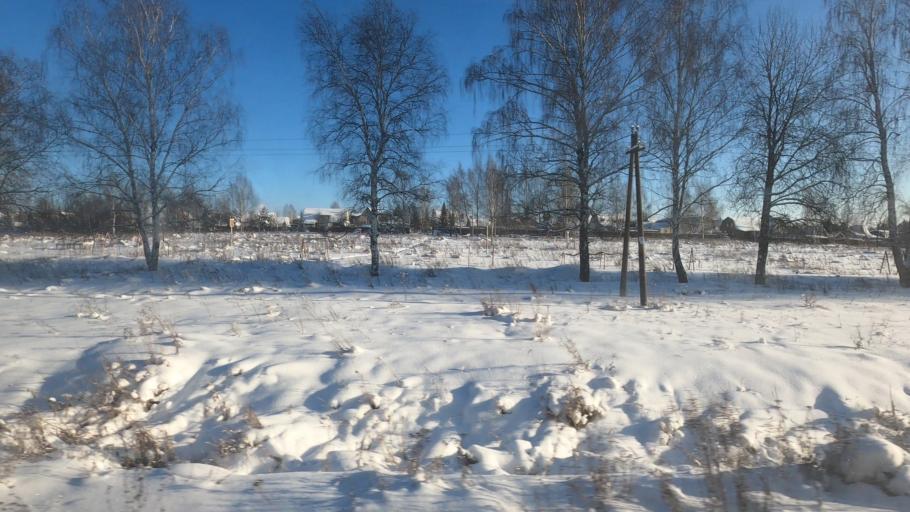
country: RU
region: Moskovskaya
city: Orud'yevo
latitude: 56.4061
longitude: 37.4950
